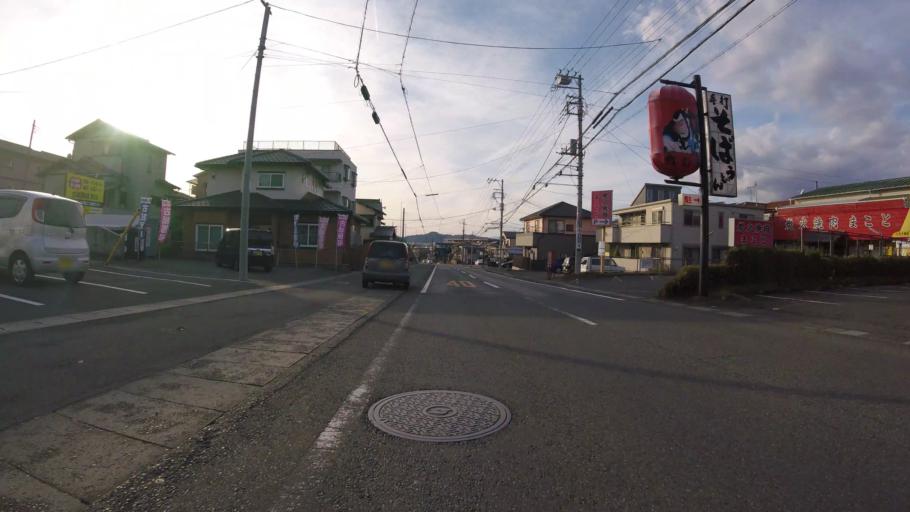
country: JP
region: Shizuoka
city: Mishima
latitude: 35.0890
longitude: 138.9517
